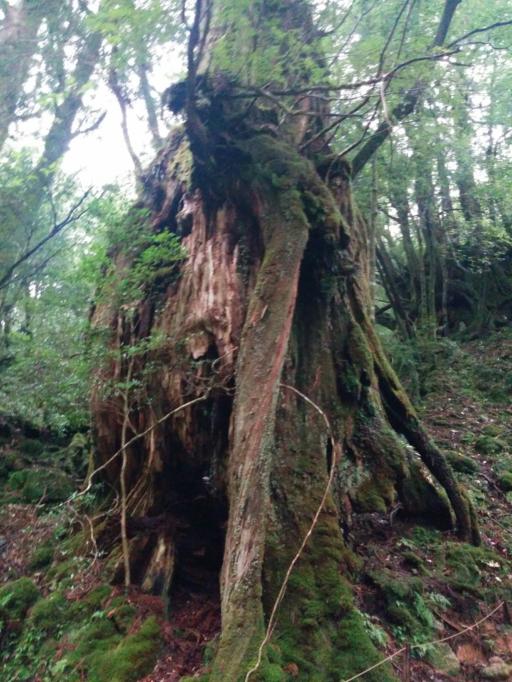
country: JP
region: Kagoshima
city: Nishinoomote
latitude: 30.3646
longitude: 130.5675
